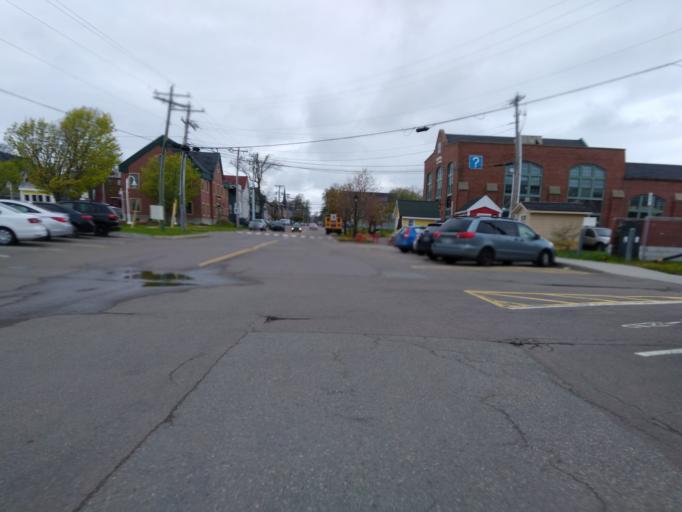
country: CA
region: Prince Edward Island
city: Charlottetown
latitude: 46.2330
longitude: -63.1205
